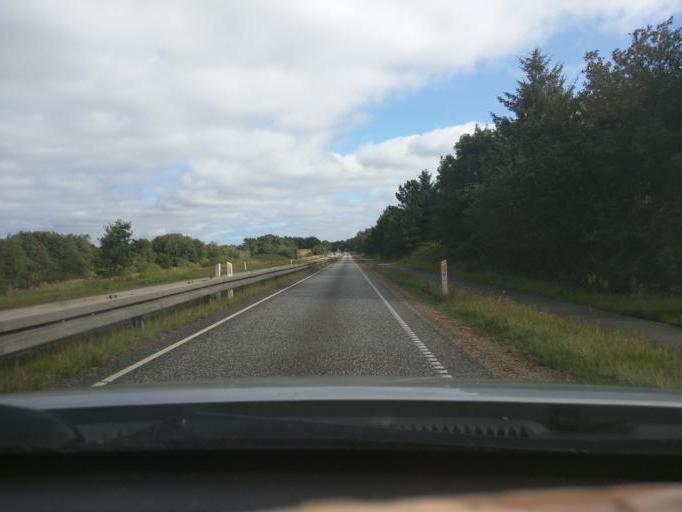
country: DK
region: Central Jutland
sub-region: Viborg Kommune
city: Viborg
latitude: 56.4205
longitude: 9.3848
